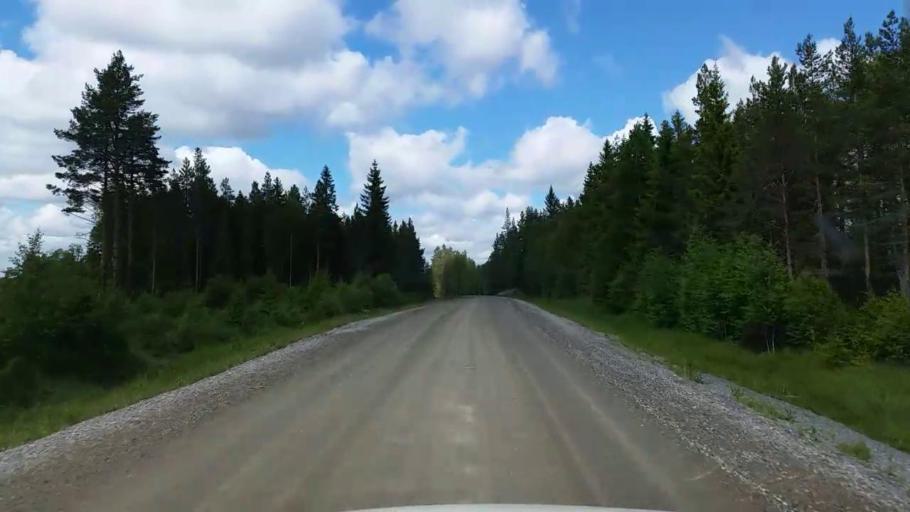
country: SE
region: Gaevleborg
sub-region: Bollnas Kommun
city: Vittsjo
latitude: 61.0572
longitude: 16.3233
